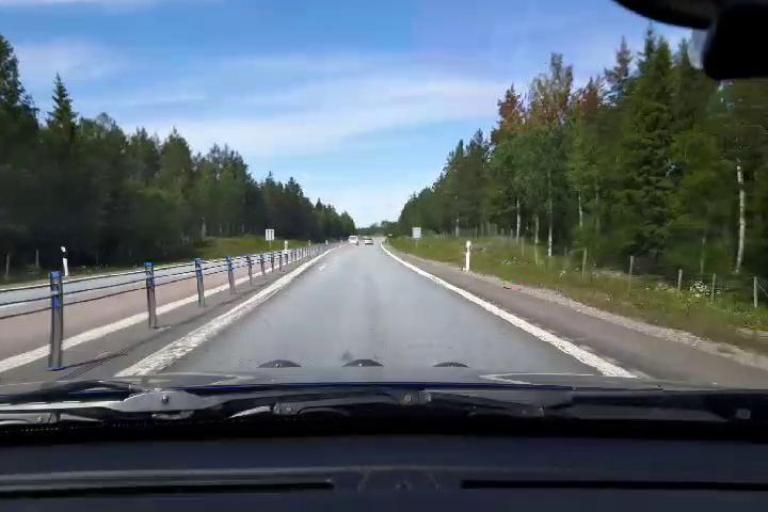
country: SE
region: Gaevleborg
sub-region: Gavle Kommun
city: Norrsundet
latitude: 60.8120
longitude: 17.0828
